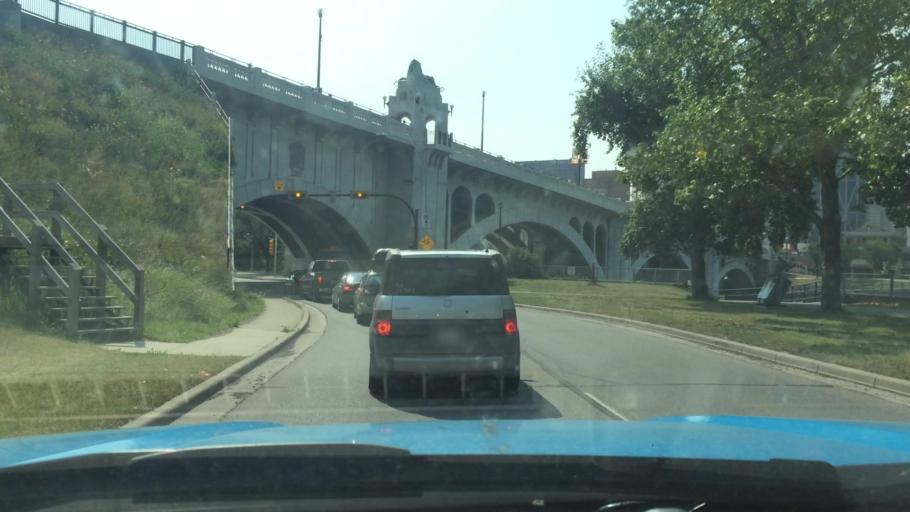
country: CA
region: Alberta
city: Calgary
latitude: 51.0543
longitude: -114.0633
